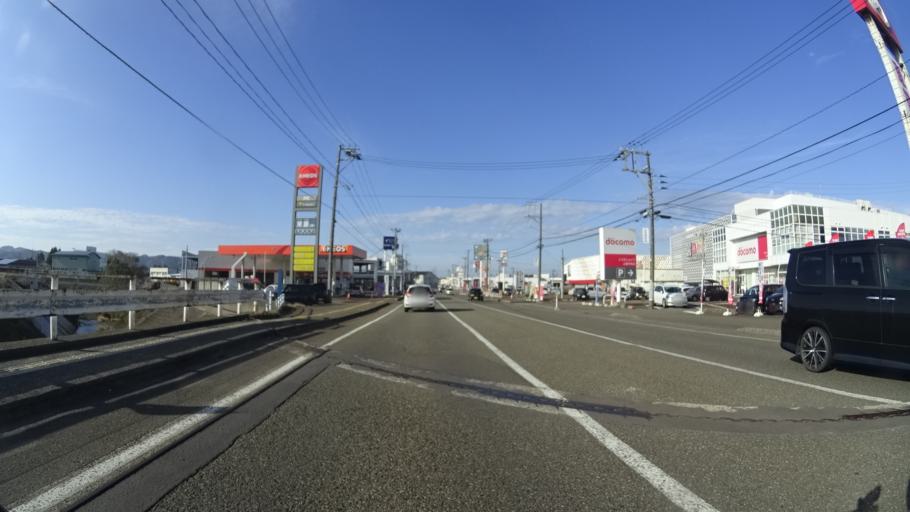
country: JP
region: Niigata
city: Joetsu
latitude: 37.1338
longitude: 138.2431
